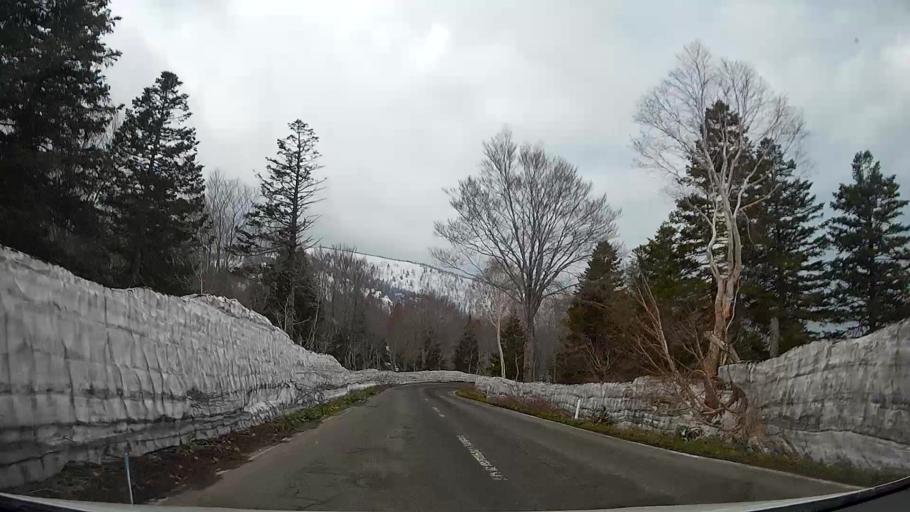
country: JP
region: Aomori
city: Aomori Shi
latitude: 40.6467
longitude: 140.8568
